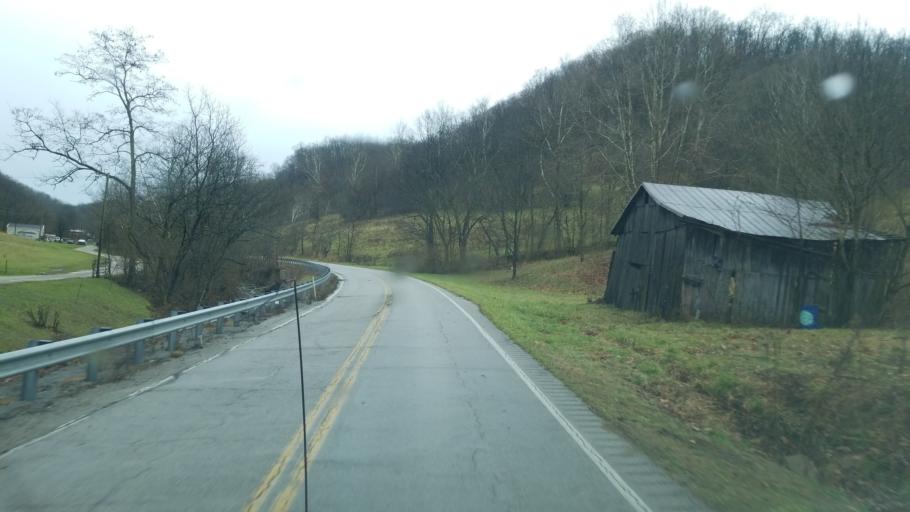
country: US
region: Kentucky
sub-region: Mason County
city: Maysville
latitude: 38.6279
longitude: -83.7072
